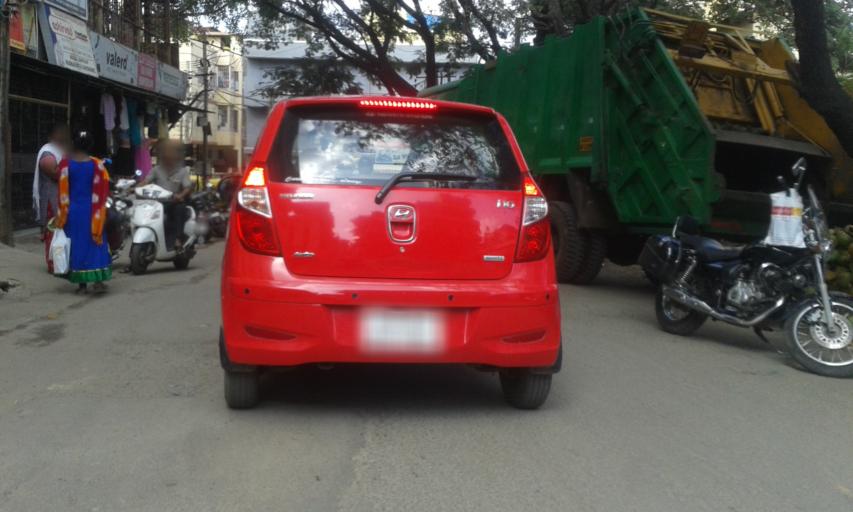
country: IN
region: Karnataka
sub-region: Bangalore Urban
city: Bangalore
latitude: 12.9431
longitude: 77.6175
